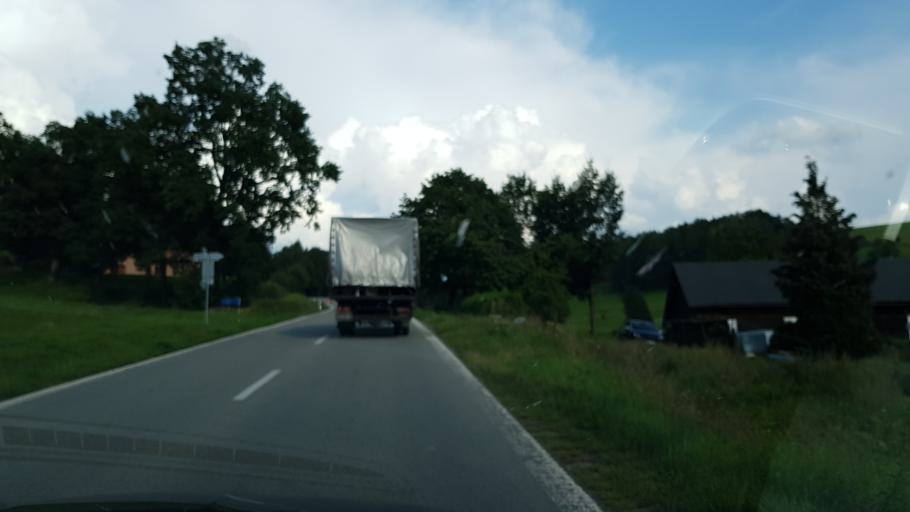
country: CZ
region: Pardubicky
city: Jablonne nad Orlici
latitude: 50.0946
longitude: 16.5695
